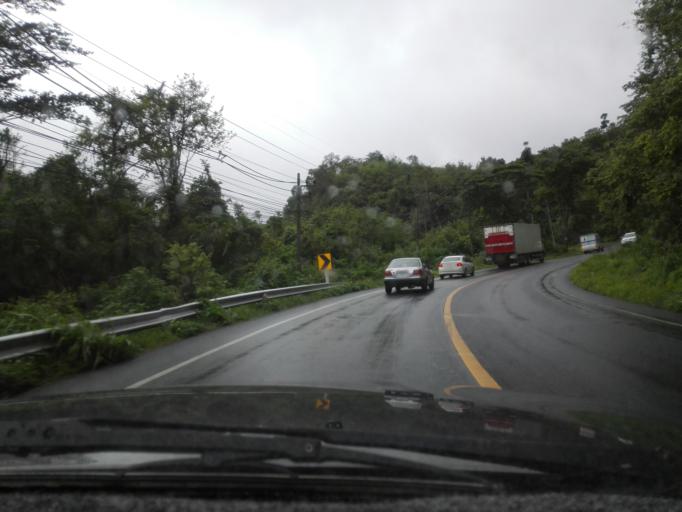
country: TH
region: Tak
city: Tak
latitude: 16.7976
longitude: 98.9519
